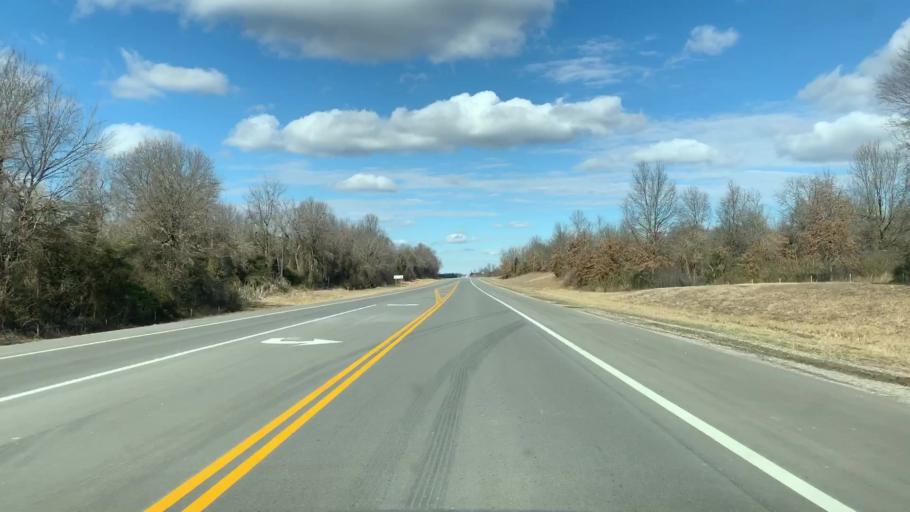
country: US
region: Kansas
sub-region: Cherokee County
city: Columbus
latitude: 37.2536
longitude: -94.8318
